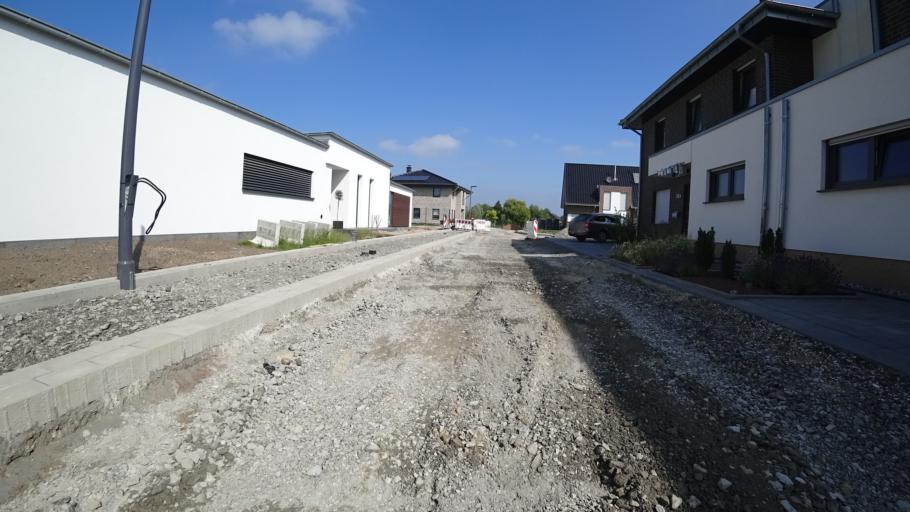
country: DE
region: North Rhine-Westphalia
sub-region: Regierungsbezirk Detmold
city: Langenberg
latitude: 51.7489
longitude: 8.3182
